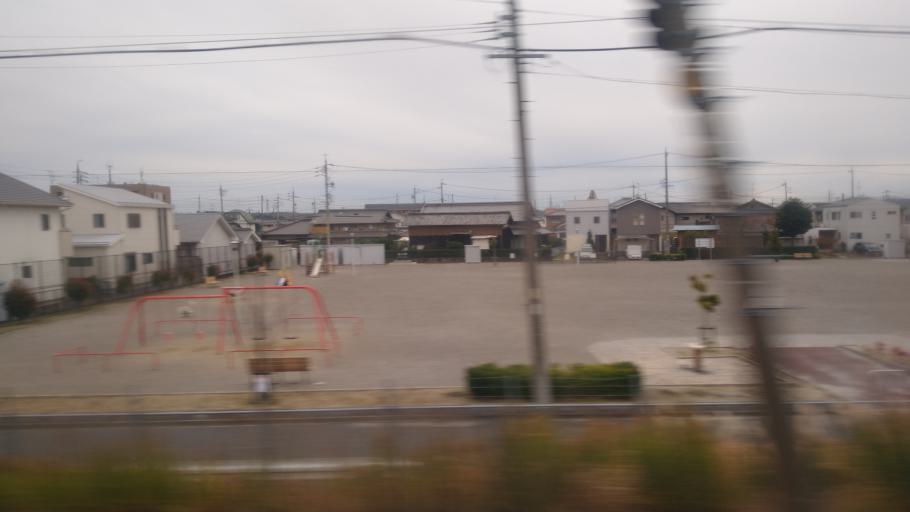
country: JP
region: Aichi
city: Kasugai
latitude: 35.2641
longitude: 137.0312
